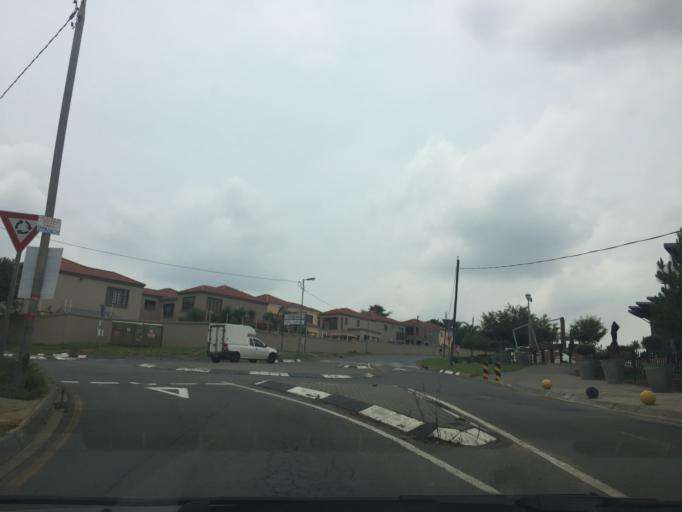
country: ZA
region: Gauteng
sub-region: City of Johannesburg Metropolitan Municipality
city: Diepsloot
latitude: -26.0165
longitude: 27.9965
